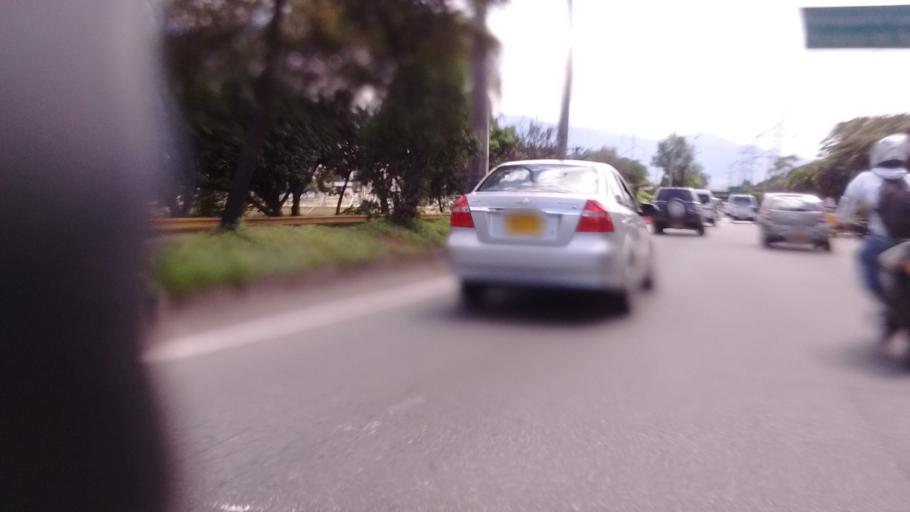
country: CO
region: Antioquia
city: Medellin
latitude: 6.2169
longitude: -75.5780
